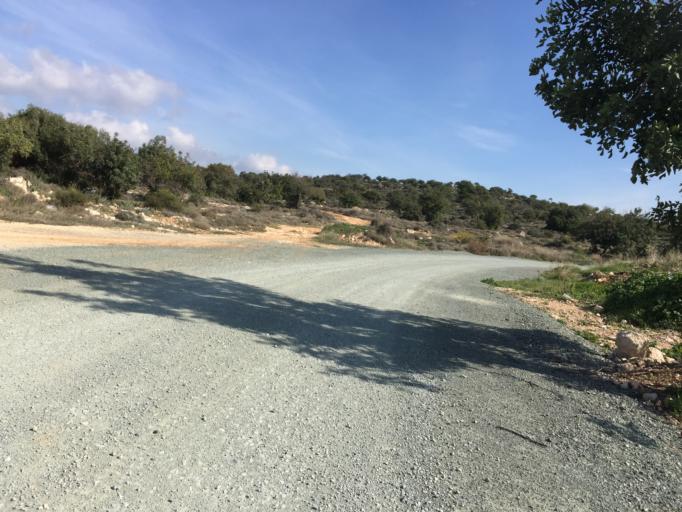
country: CY
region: Larnaka
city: Agios Tychon
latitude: 34.7420
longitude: 33.1218
